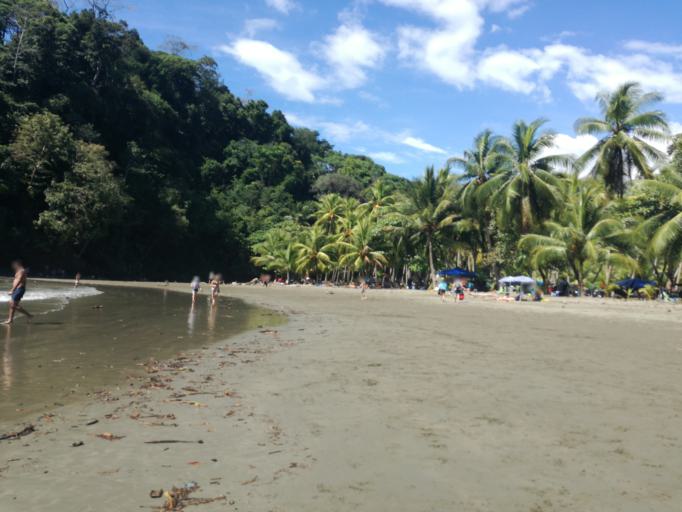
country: CR
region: San Jose
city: Mercedes
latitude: 9.0910
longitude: -83.6773
